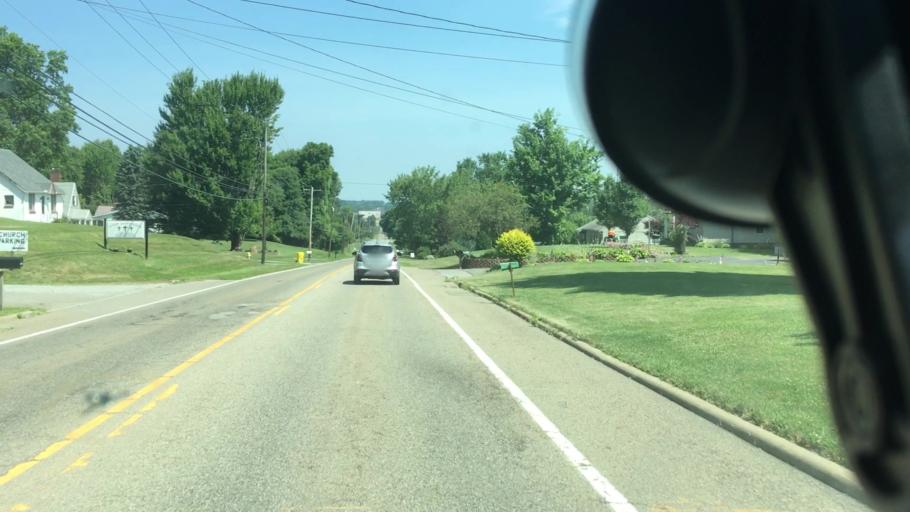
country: US
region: Ohio
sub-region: Columbiana County
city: Salem
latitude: 40.8805
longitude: -80.8570
